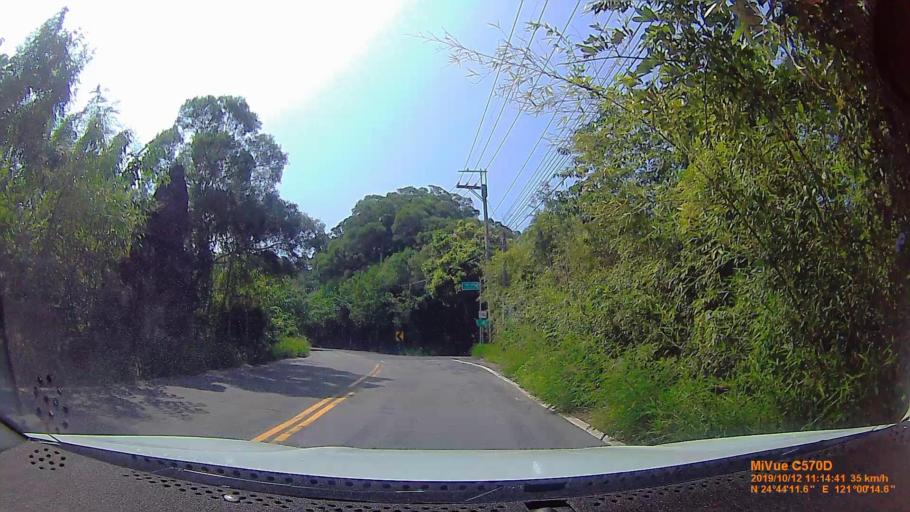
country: TW
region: Taiwan
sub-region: Hsinchu
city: Hsinchu
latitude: 24.7365
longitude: 121.0040
